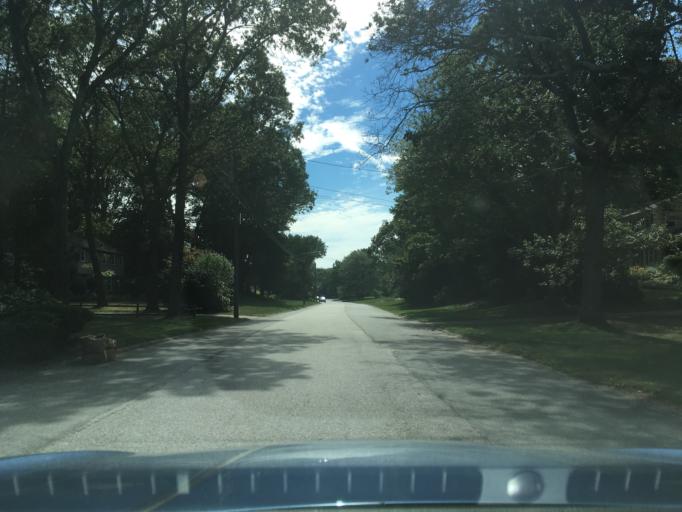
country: US
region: Rhode Island
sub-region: Kent County
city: East Greenwich
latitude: 41.6553
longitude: -71.4674
